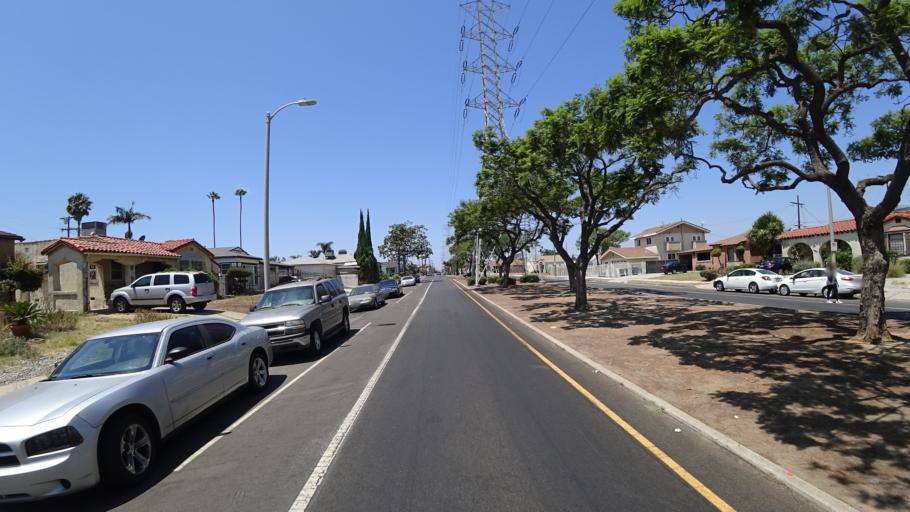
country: US
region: California
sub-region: Los Angeles County
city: Westmont
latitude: 33.9468
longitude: -118.3038
